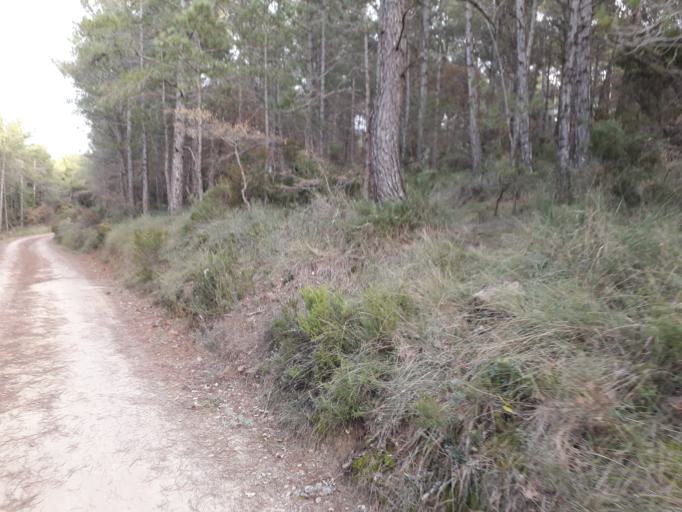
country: ES
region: Catalonia
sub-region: Provincia de Barcelona
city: Sant Marti de Tous
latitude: 41.5738
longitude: 1.4867
